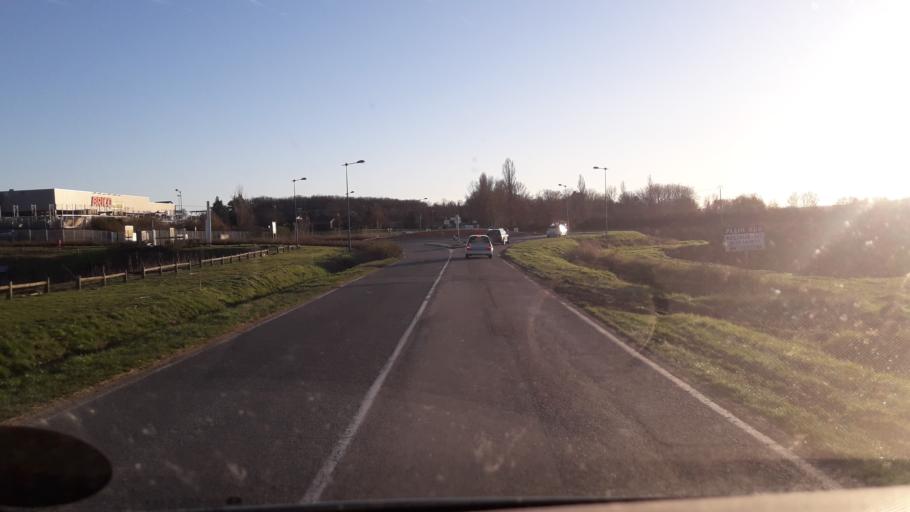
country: FR
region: Midi-Pyrenees
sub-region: Departement du Gers
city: Pujaudran
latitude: 43.6021
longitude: 1.0677
